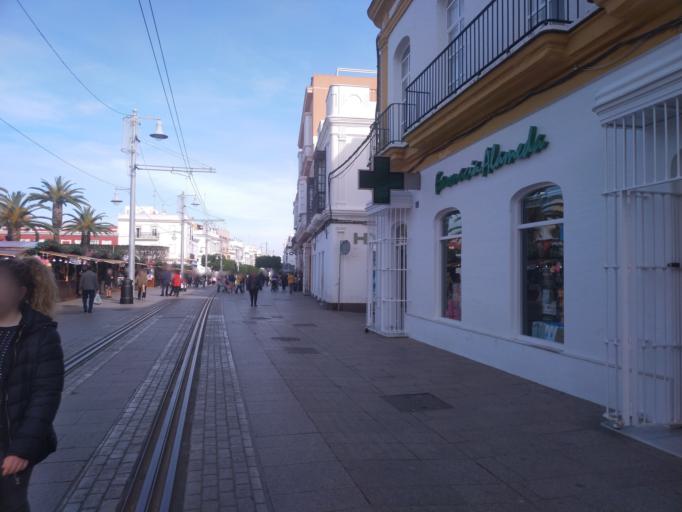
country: ES
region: Andalusia
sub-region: Provincia de Cadiz
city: San Fernando
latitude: 36.4624
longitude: -6.1996
